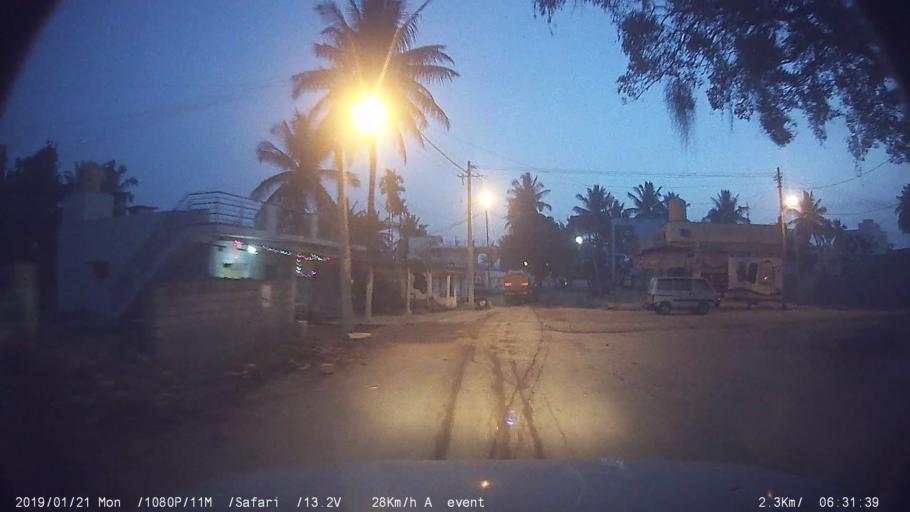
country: IN
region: Karnataka
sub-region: Bangalore Urban
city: Anekal
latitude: 12.8187
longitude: 77.6371
